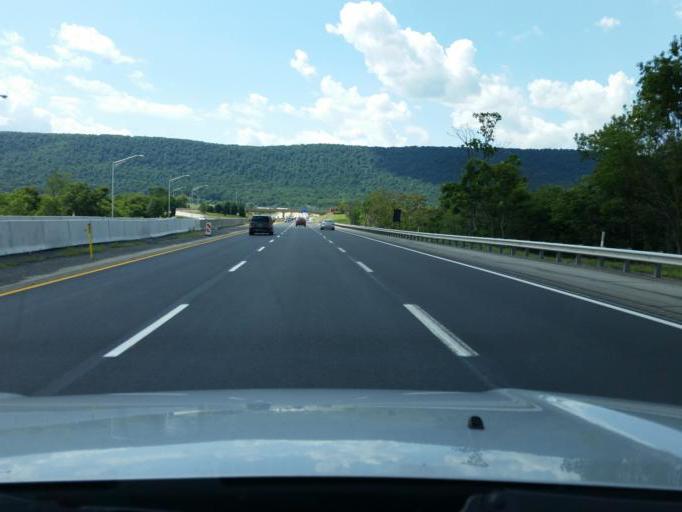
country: US
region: Pennsylvania
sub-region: Fulton County
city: McConnellsburg
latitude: 40.0544
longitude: -78.0754
